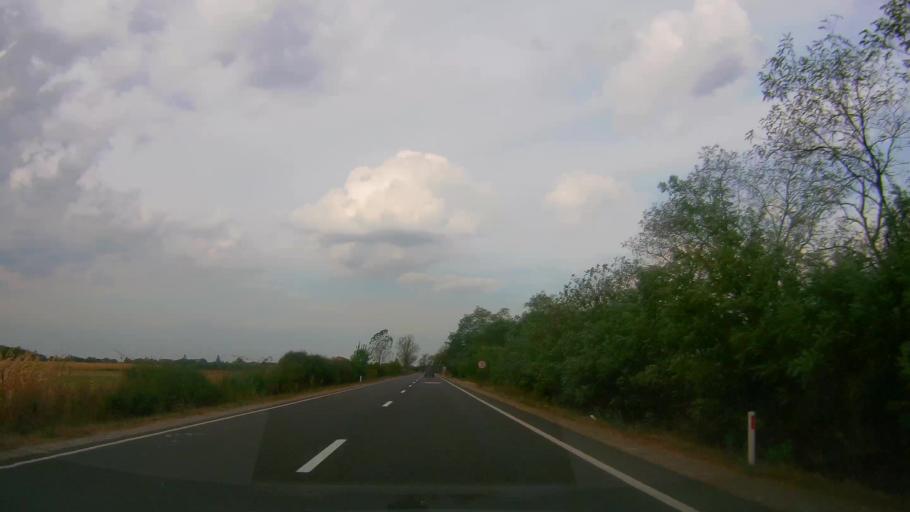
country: RO
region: Satu Mare
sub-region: Comuna Acas
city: Acas
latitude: 47.5402
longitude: 22.7958
